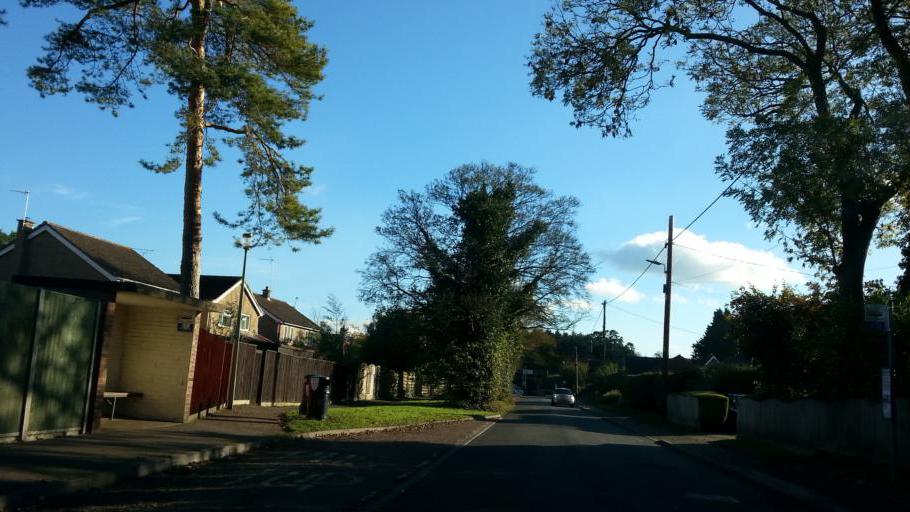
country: GB
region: England
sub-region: Suffolk
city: Thurston
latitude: 52.2518
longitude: 0.8066
